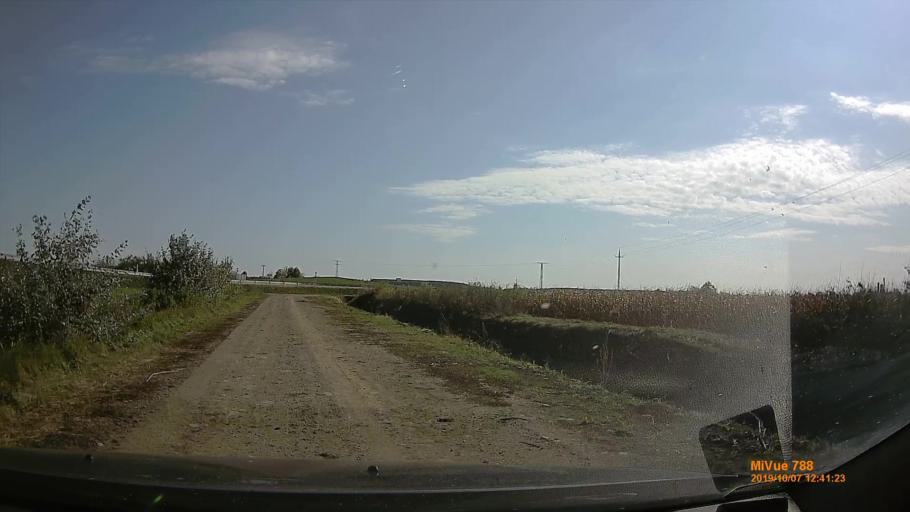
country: HU
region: Jasz-Nagykun-Szolnok
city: Kunszentmarton
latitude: 46.8699
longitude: 20.2628
